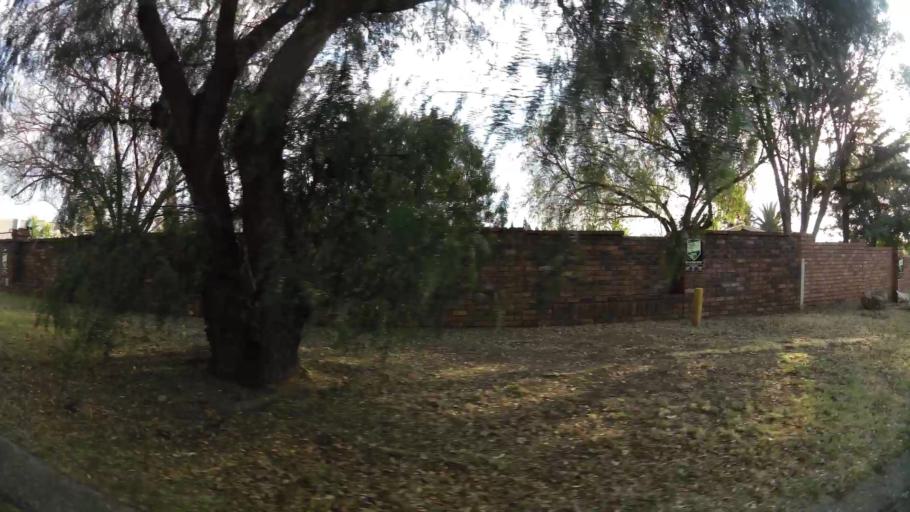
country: ZA
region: Gauteng
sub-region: City of Johannesburg Metropolitan Municipality
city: Modderfontein
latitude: -26.1260
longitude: 28.1892
